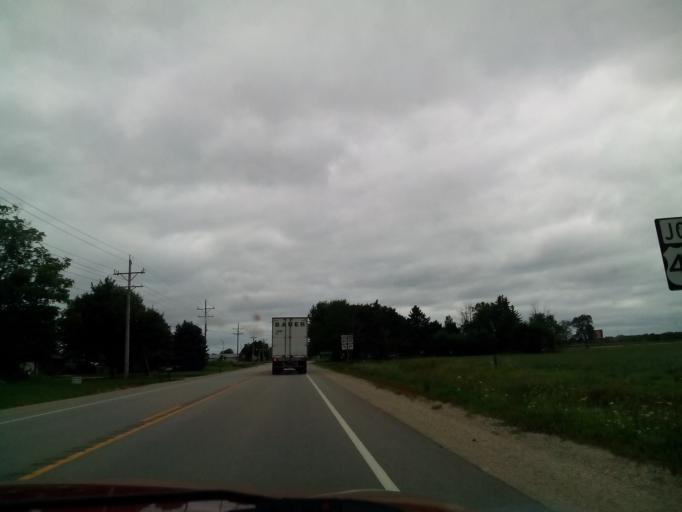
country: US
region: Wisconsin
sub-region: Outagamie County
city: Hortonville
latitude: 44.2724
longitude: -88.7358
